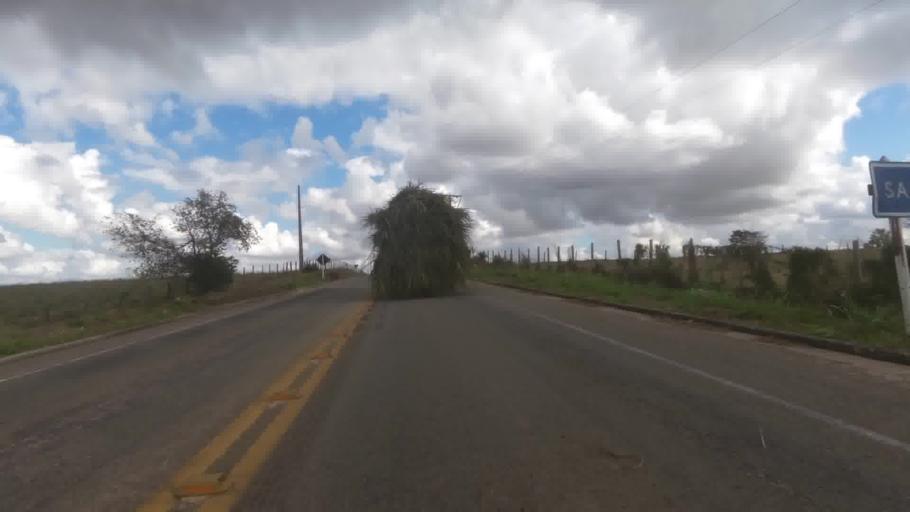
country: BR
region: Espirito Santo
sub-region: Marataizes
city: Marataizes
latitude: -21.1844
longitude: -40.9798
